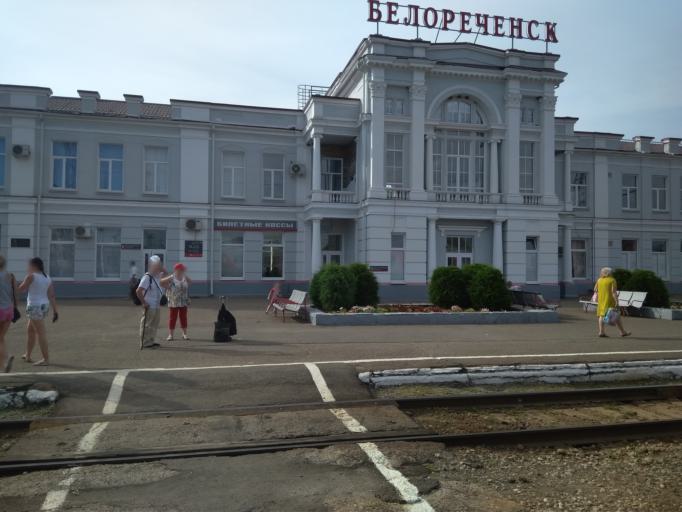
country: RU
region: Krasnodarskiy
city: Belorechensk
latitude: 44.7527
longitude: 39.8939
